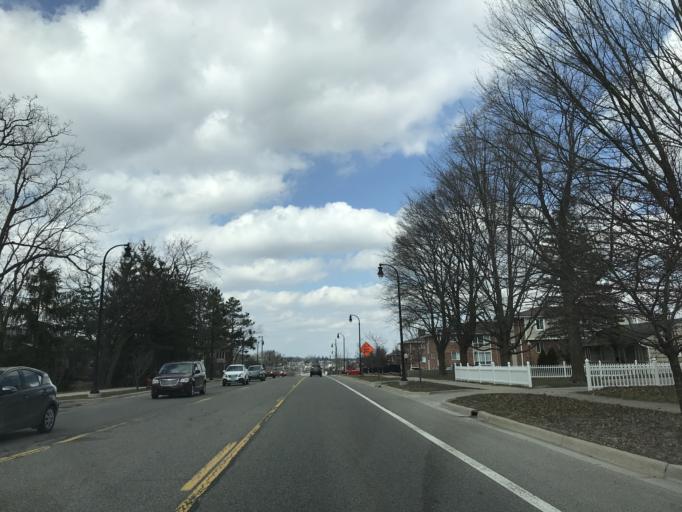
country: US
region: Michigan
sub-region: Washtenaw County
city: Ann Arbor
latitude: 42.2654
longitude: -83.7685
